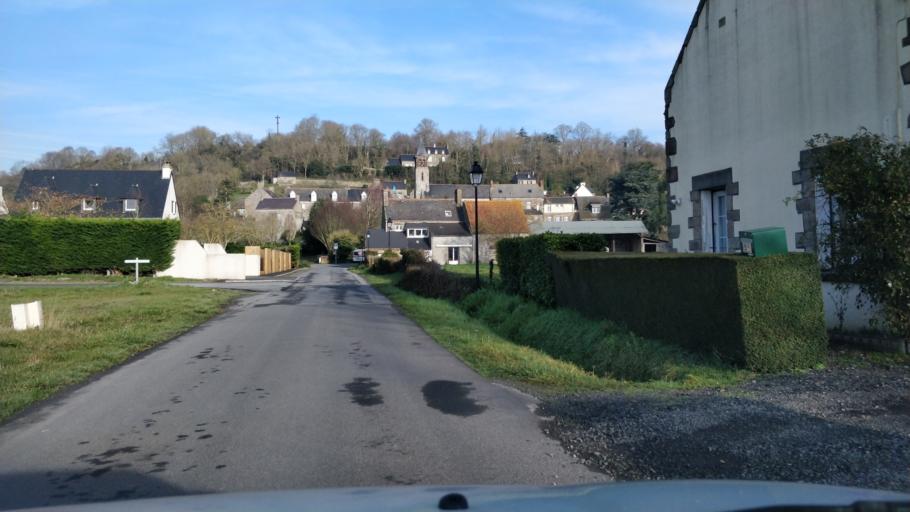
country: FR
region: Brittany
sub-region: Departement d'Ille-et-Vilaine
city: Dol-de-Bretagne
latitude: 48.5680
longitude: -1.7678
